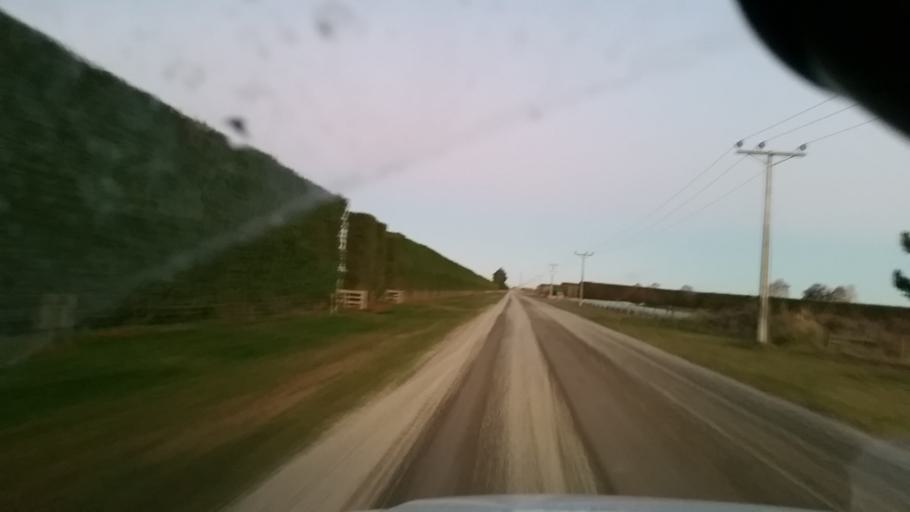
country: NZ
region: Canterbury
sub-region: Ashburton District
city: Tinwald
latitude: -43.9716
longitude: 171.6379
